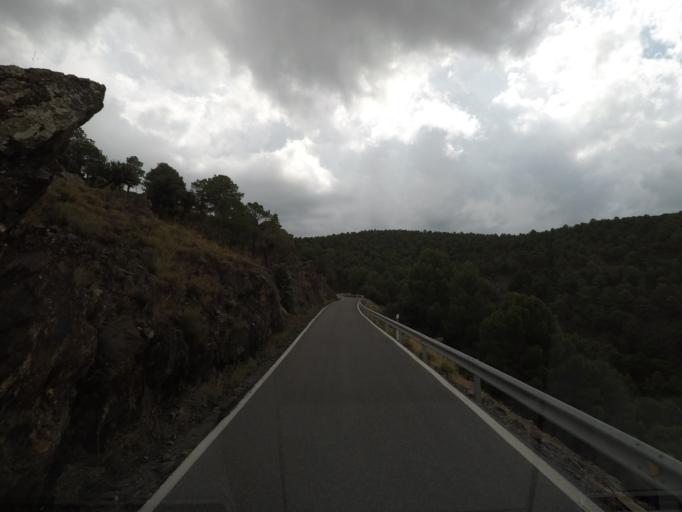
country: ES
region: Andalusia
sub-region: Provincia de Granada
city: Ferreira
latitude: 37.1636
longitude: -3.0517
